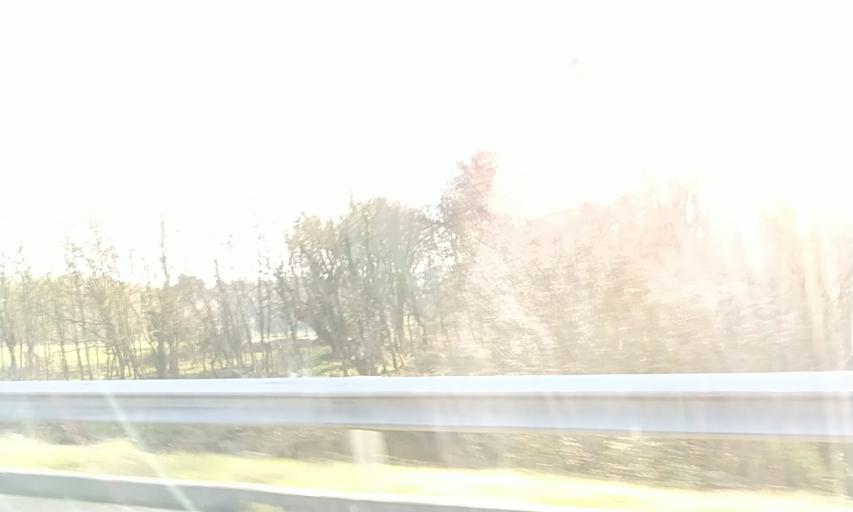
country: ES
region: Galicia
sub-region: Provincia de Lugo
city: Lugo
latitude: 42.9865
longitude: -7.5025
